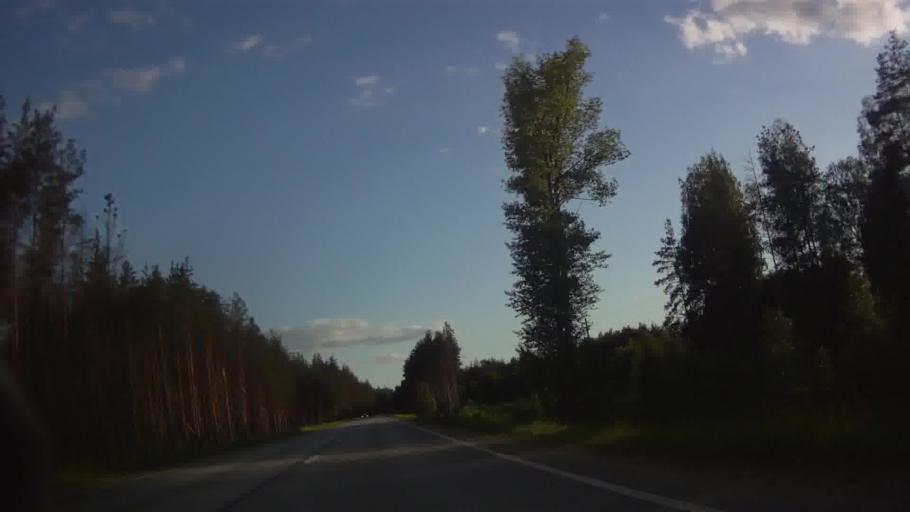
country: LV
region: Varaklani
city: Varaklani
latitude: 56.5496
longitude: 26.5906
